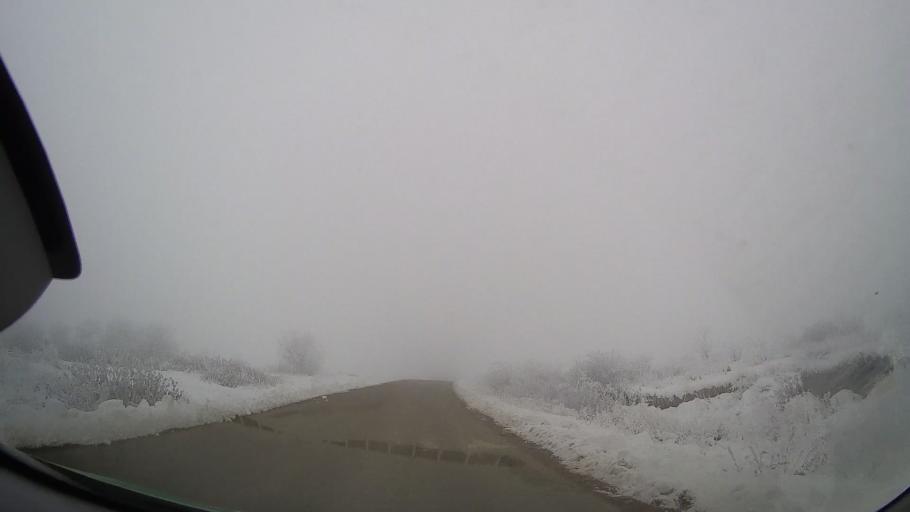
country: RO
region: Iasi
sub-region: Comuna Tansa
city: Suhulet
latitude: 46.8886
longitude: 27.2702
